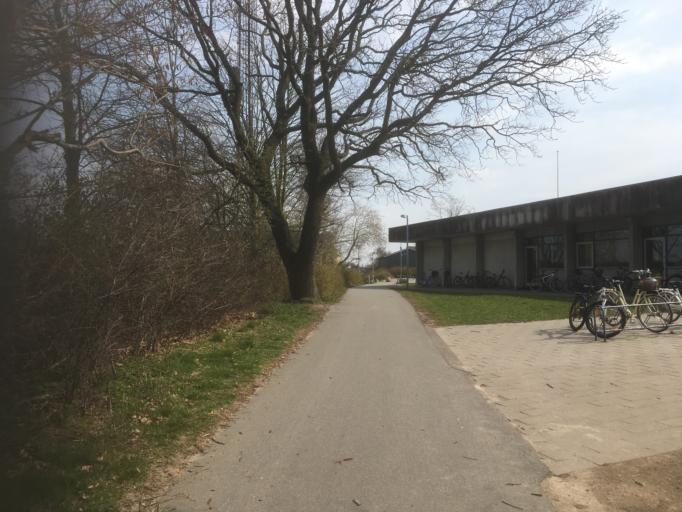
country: DK
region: South Denmark
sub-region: Nordfyns Kommune
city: Sonderso
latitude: 55.4214
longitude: 10.2651
